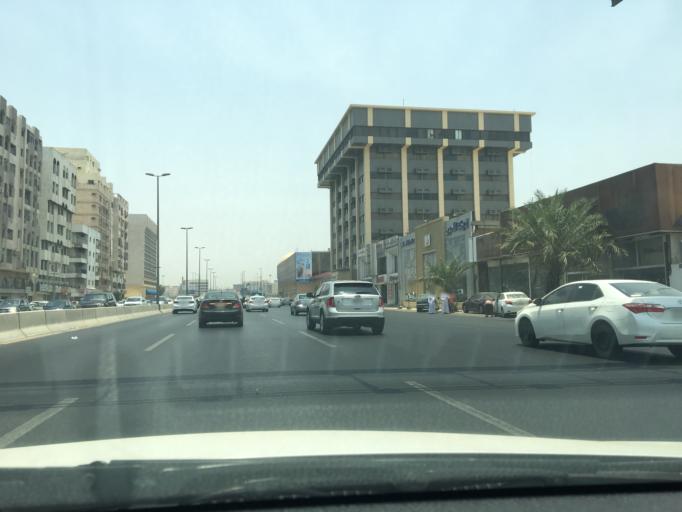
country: SA
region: Makkah
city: Jeddah
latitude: 21.5264
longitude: 39.1926
